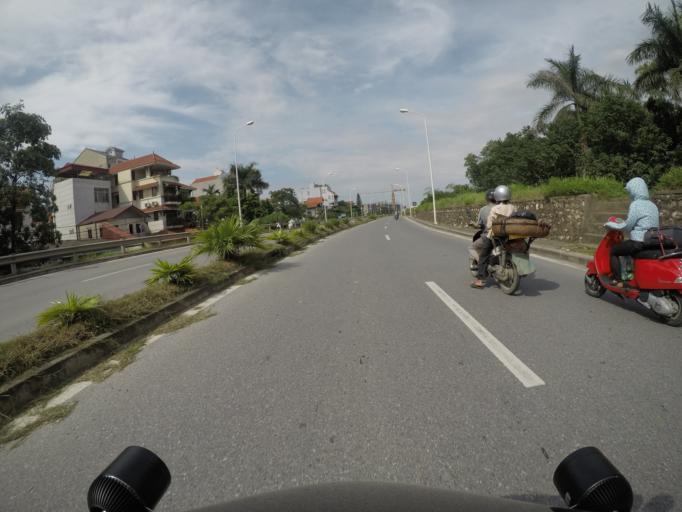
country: VN
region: Ha Noi
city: Tay Ho
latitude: 21.0893
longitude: 105.7980
